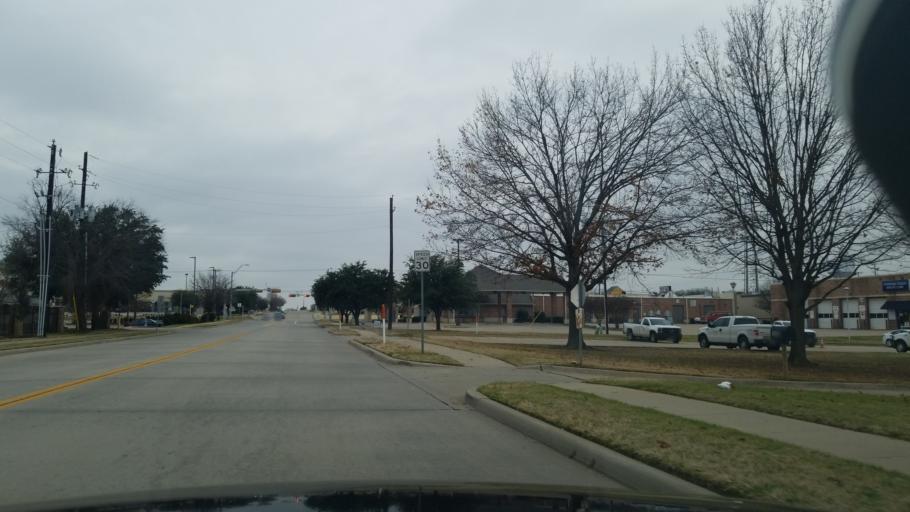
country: US
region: Texas
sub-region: Denton County
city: Hickory Creek
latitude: 33.1315
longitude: -97.0474
